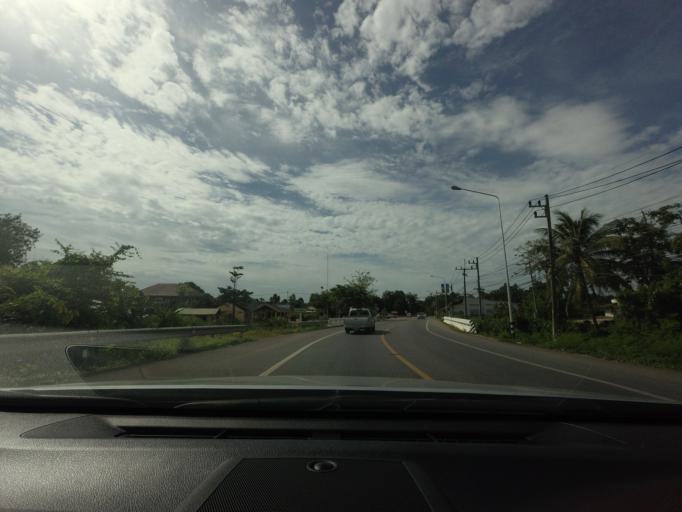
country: TH
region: Songkhla
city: Khlong Hoi Khong
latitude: 6.9215
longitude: 100.4106
